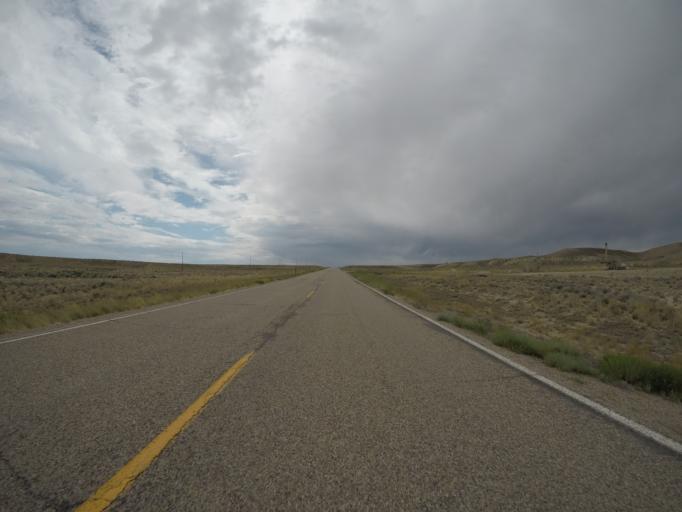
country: US
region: Wyoming
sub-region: Lincoln County
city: Kemmerer
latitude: 41.9717
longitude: -110.0825
